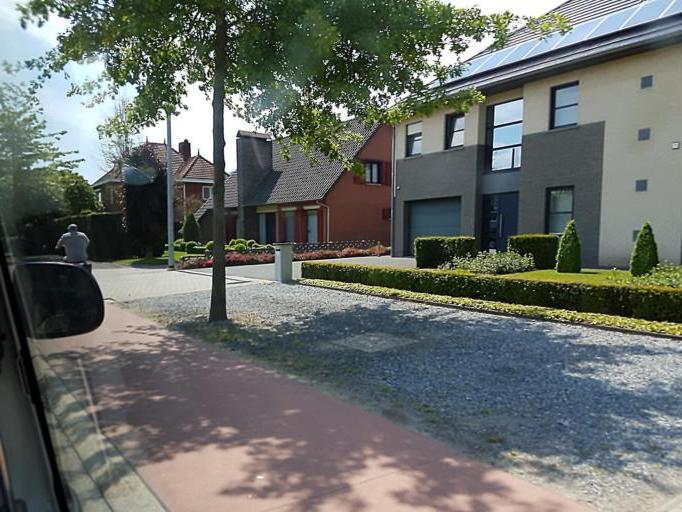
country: BE
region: Flanders
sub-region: Provincie Limburg
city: Neerpelt
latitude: 51.2240
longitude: 5.4803
